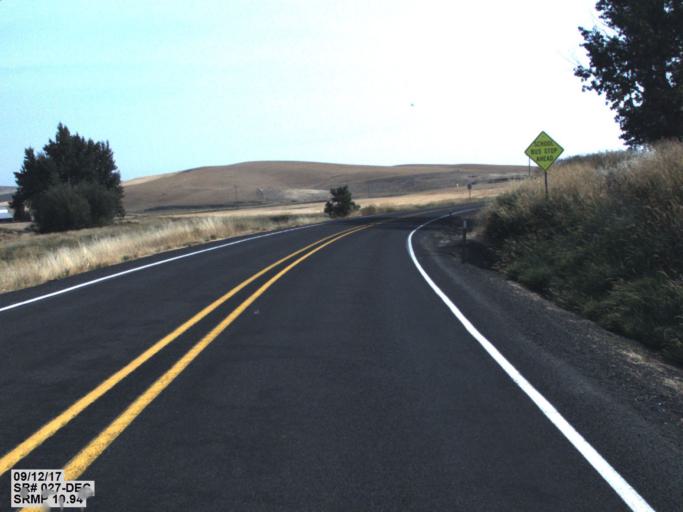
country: US
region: Washington
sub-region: Whitman County
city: Pullman
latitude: 46.9628
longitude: -117.1007
